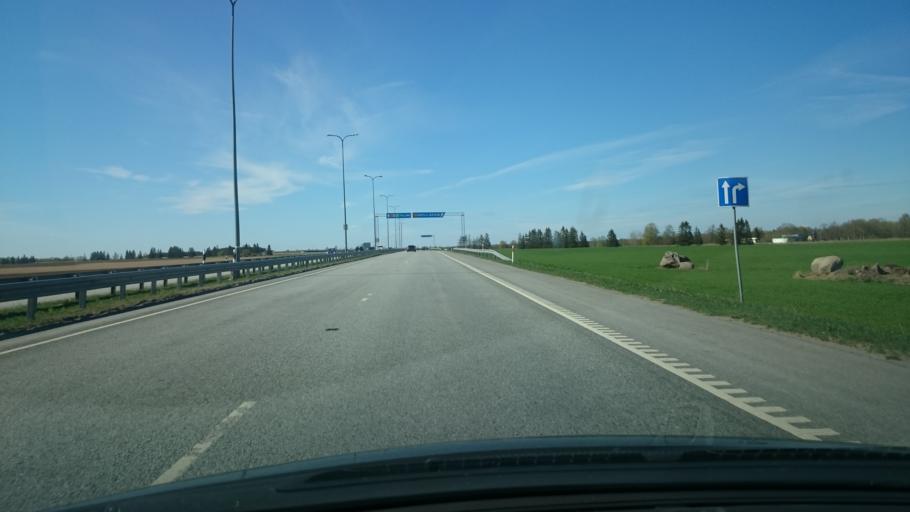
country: EE
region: Ida-Virumaa
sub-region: Kohtla-Jaerve linn
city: Kohtla-Jarve
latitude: 59.3952
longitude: 27.3353
